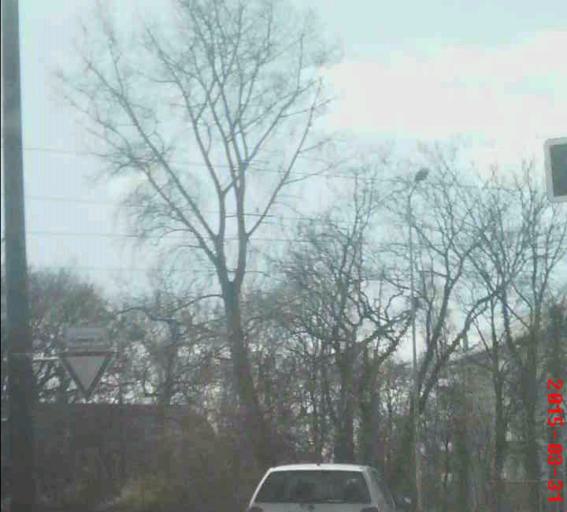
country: DE
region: Thuringia
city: Erfurt
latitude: 51.0039
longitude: 11.0214
